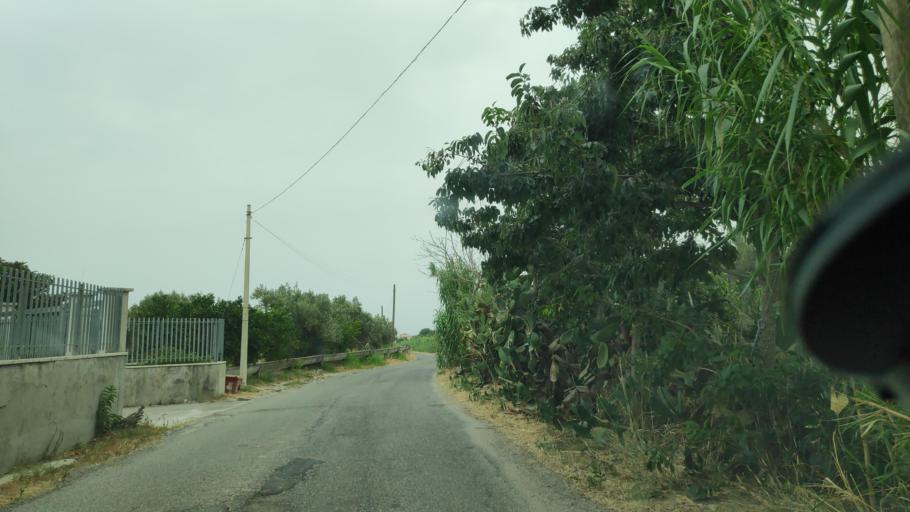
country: IT
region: Calabria
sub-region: Provincia di Catanzaro
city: Marina di Davoli
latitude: 38.6627
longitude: 16.5330
